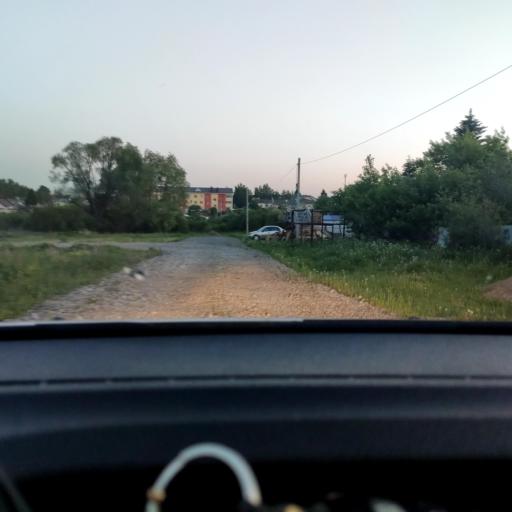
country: RU
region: Bashkortostan
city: Mikhaylovka
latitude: 54.8175
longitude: 55.8039
